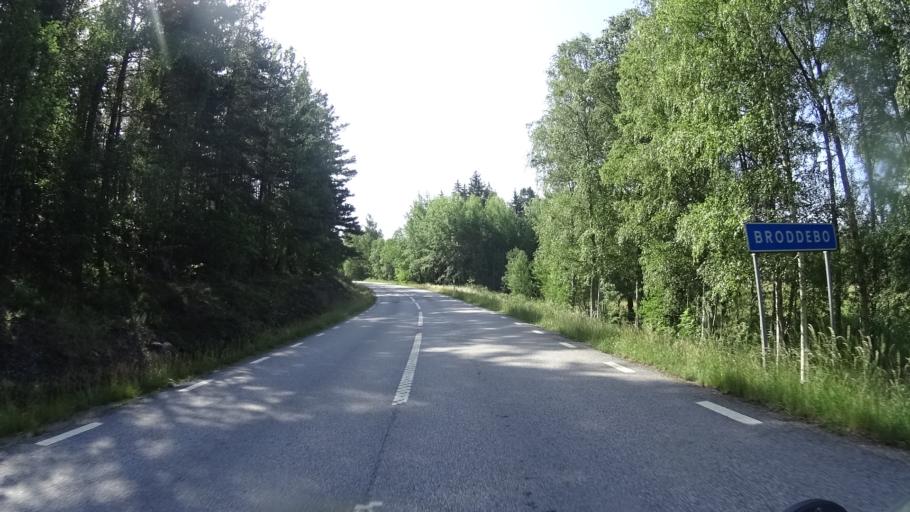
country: SE
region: Kalmar
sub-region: Vasterviks Kommun
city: Overum
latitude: 58.0810
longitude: 16.1519
